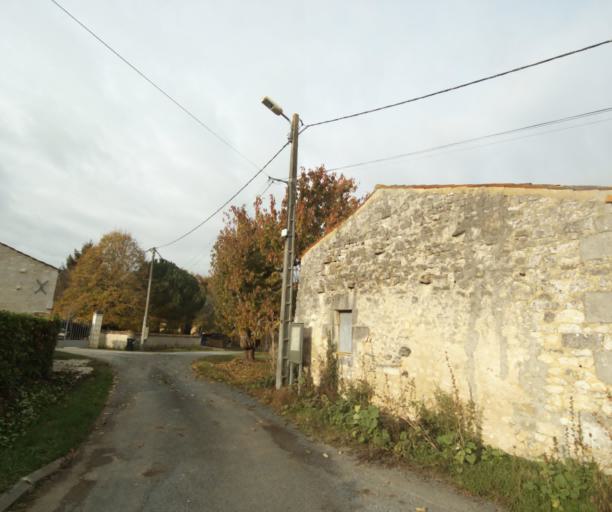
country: FR
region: Poitou-Charentes
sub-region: Departement de la Charente-Maritime
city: Nieul-les-Saintes
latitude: 45.7820
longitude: -0.7414
